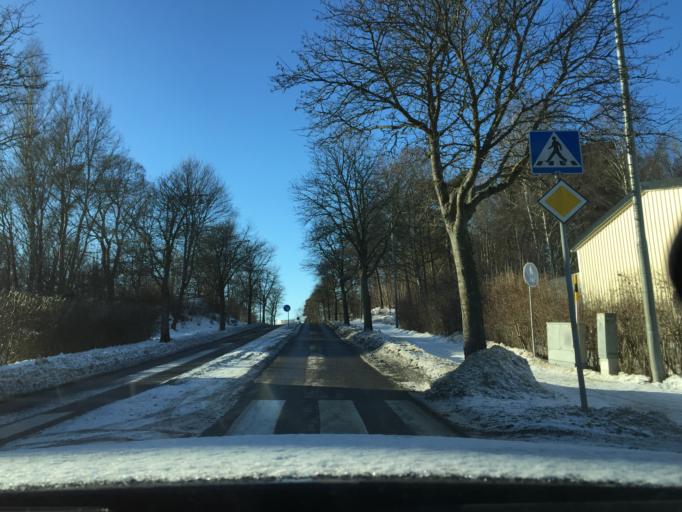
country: SE
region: Stockholm
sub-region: Stockholms Kommun
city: Bromma
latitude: 59.3504
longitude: 17.8989
